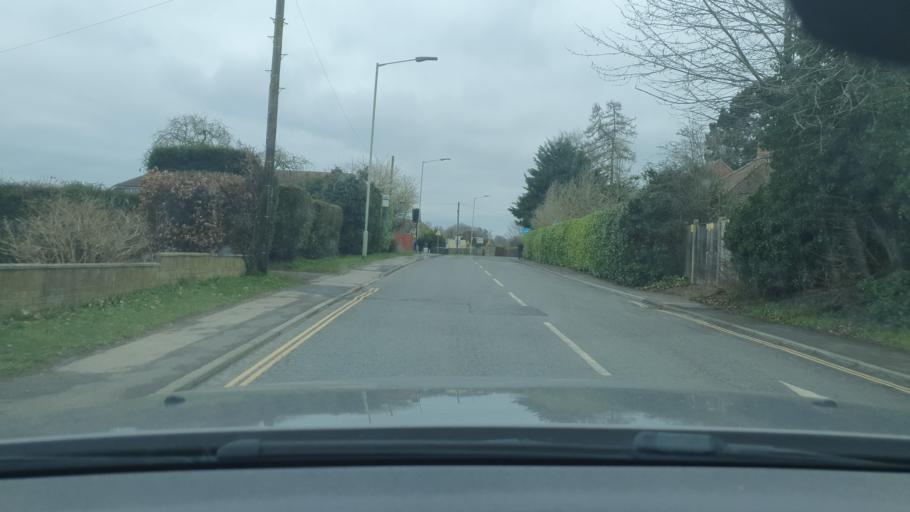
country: GB
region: England
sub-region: West Berkshire
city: Tilehurst
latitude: 51.4775
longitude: -1.0522
